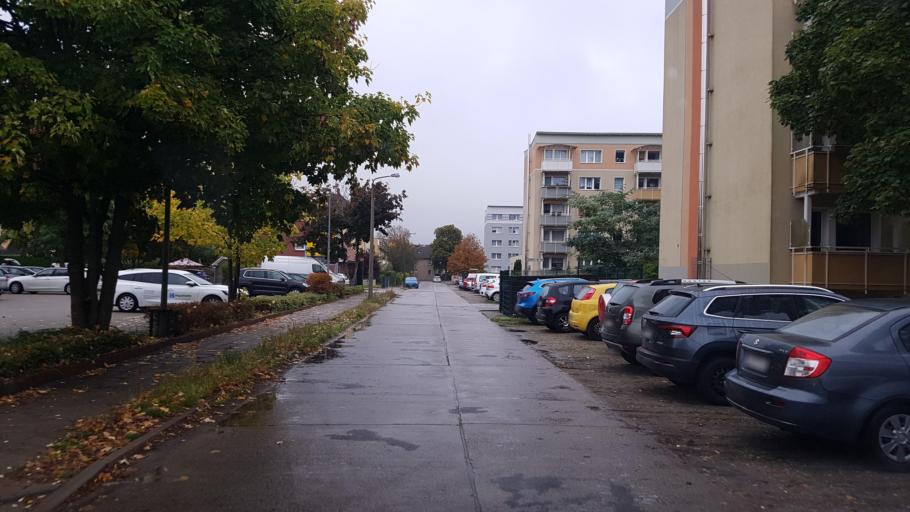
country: DE
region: Brandenburg
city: Furstenwalde
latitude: 52.3760
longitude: 14.0589
